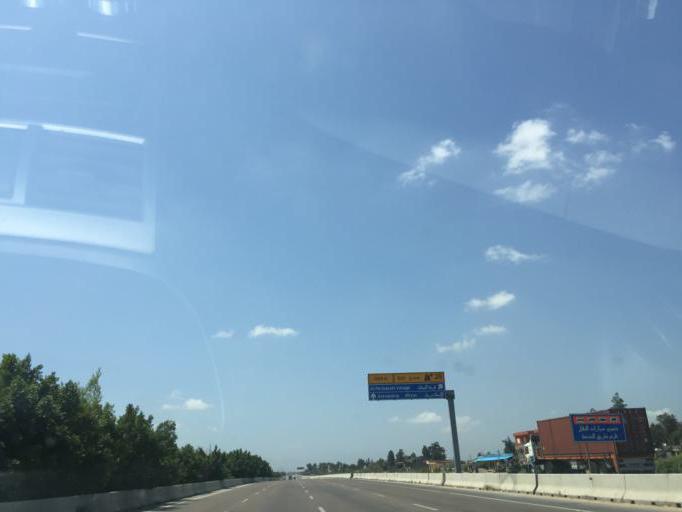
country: EG
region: Alexandria
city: Alexandria
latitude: 30.9473
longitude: 29.8429
